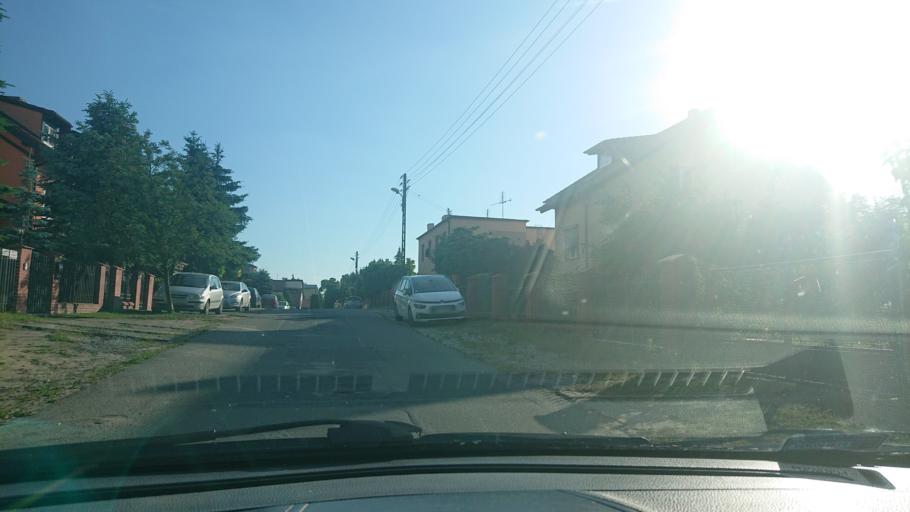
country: PL
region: Greater Poland Voivodeship
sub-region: Powiat gnieznienski
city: Gniezno
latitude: 52.5213
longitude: 17.6110
